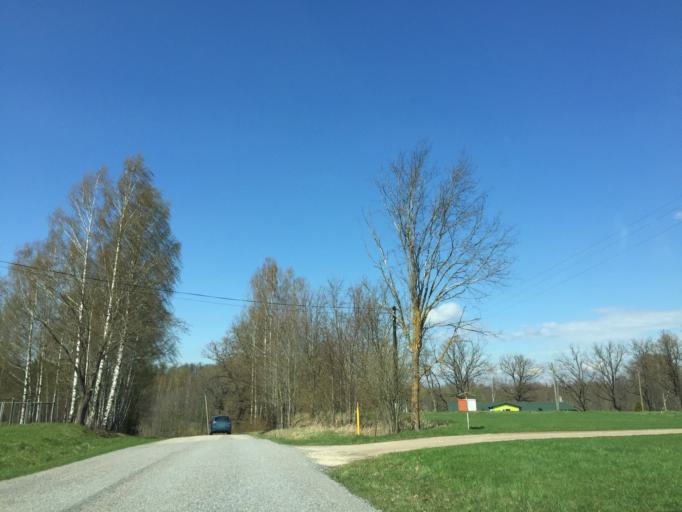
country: EE
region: Tartu
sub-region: Elva linn
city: Elva
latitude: 58.1503
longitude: 26.2323
